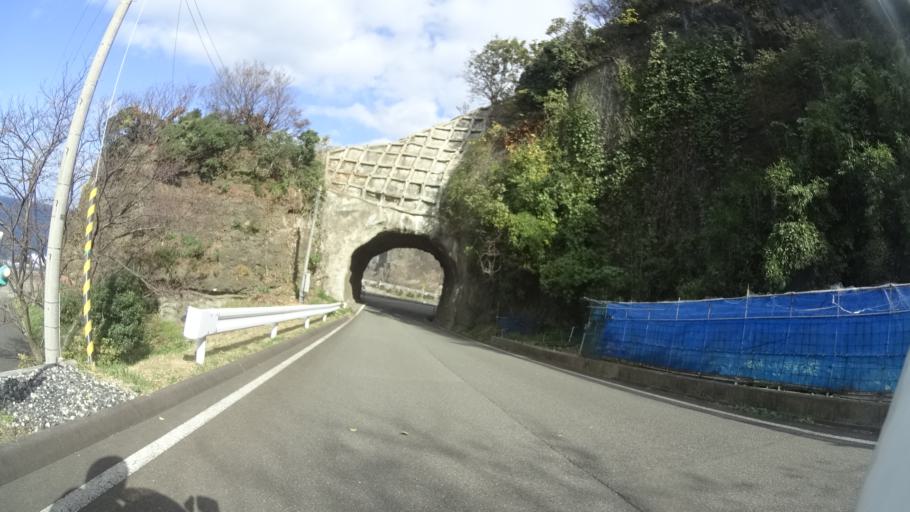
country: JP
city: Asahi
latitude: 35.9842
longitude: 135.9605
